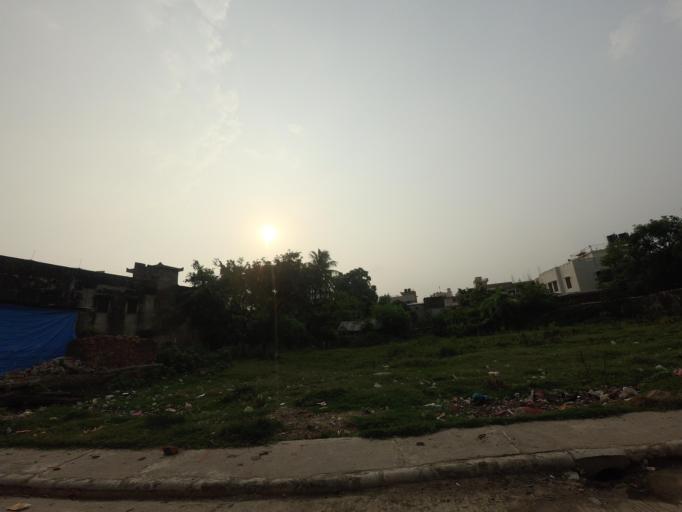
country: NP
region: Western Region
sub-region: Lumbini Zone
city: Bhairahawa
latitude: 27.5042
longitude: 83.4493
